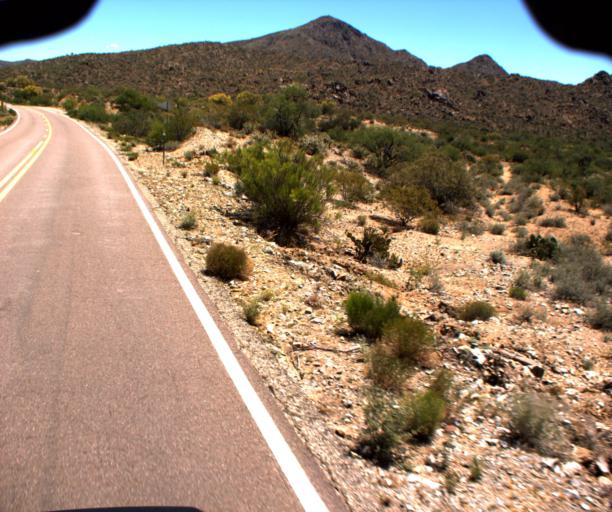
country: US
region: Arizona
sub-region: Yavapai County
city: Bagdad
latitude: 34.4612
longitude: -113.2354
